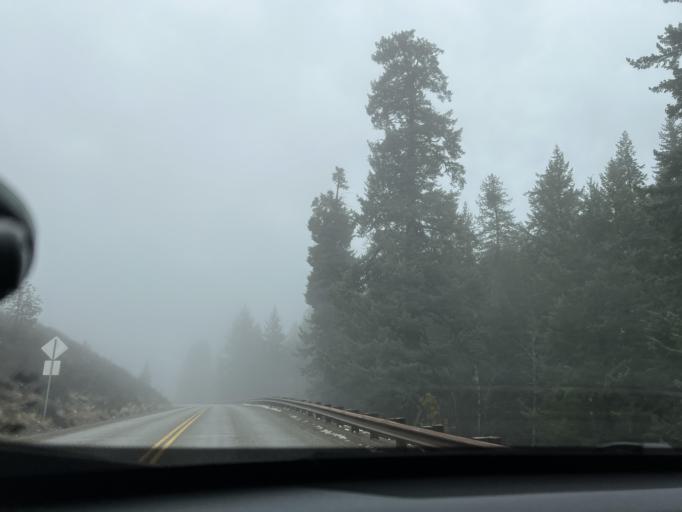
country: US
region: Washington
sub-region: Chelan County
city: Granite Falls
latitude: 48.4352
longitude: -120.2205
